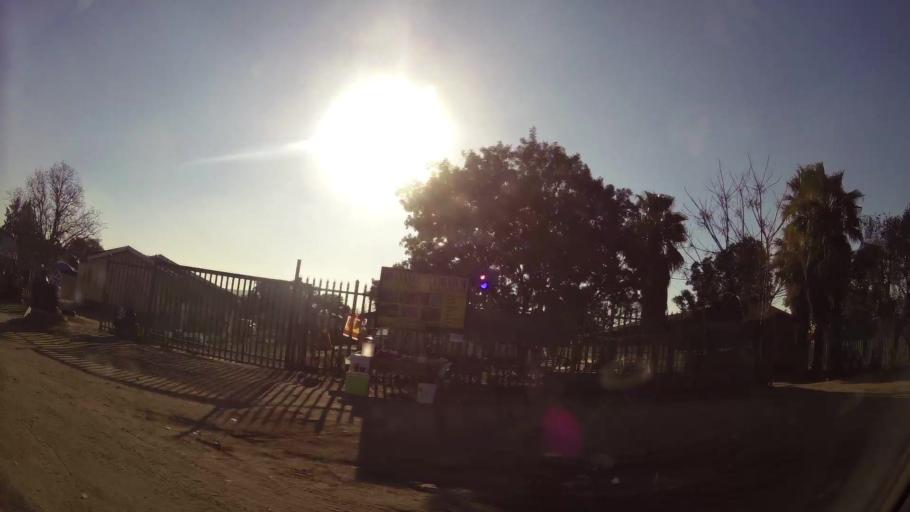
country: ZA
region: North-West
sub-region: Bojanala Platinum District Municipality
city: Rustenburg
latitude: -25.6603
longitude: 27.2659
